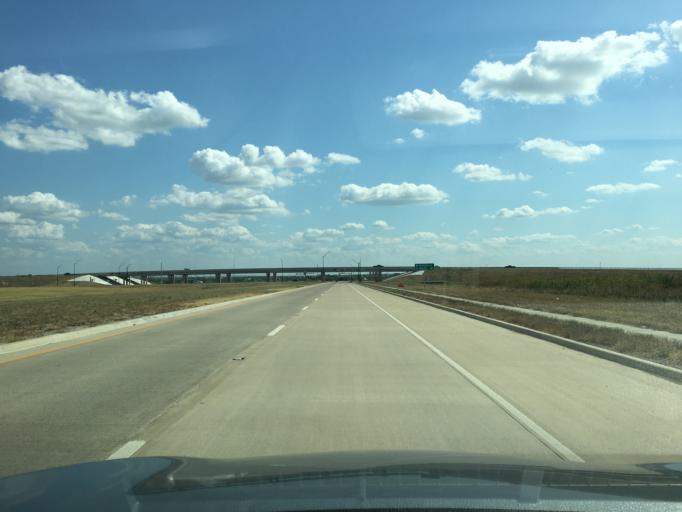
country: US
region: Texas
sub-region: Tarrant County
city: Mansfield
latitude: 32.5261
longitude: -97.0830
